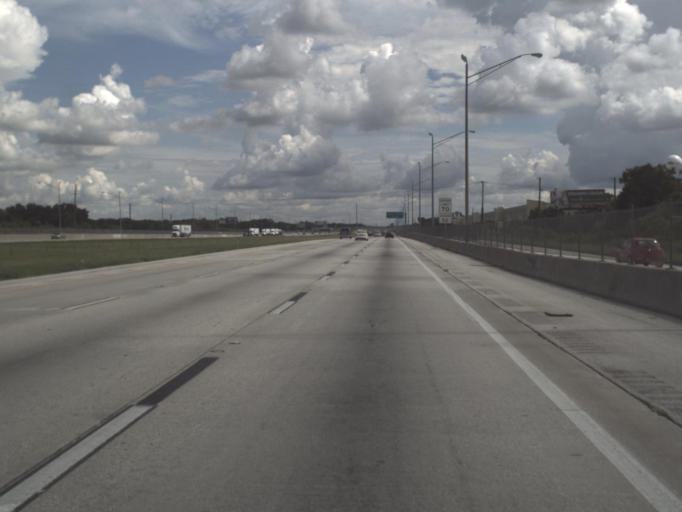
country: US
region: Florida
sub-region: Polk County
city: Winston
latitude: 28.0390
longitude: -82.0324
